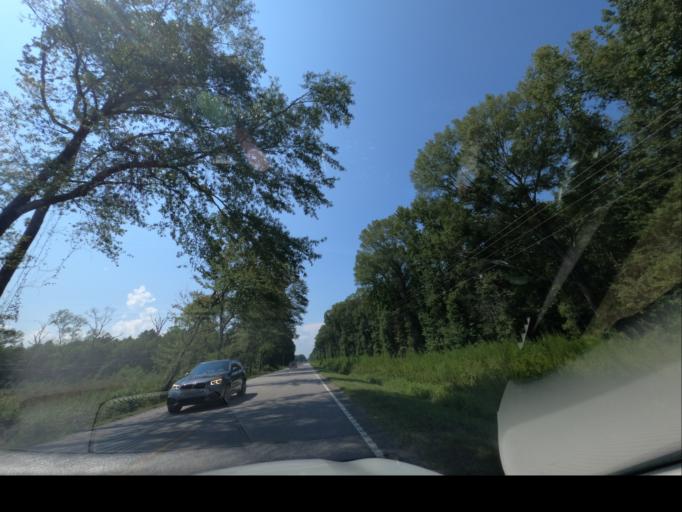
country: US
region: South Carolina
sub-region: Richland County
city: Hopkins
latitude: 33.8829
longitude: -80.9061
